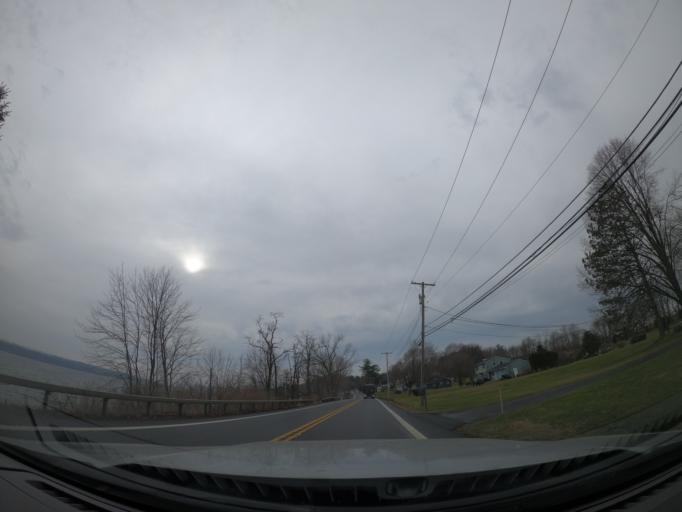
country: US
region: New York
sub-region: Cayuga County
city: Melrose Park
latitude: 42.8588
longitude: -76.5312
